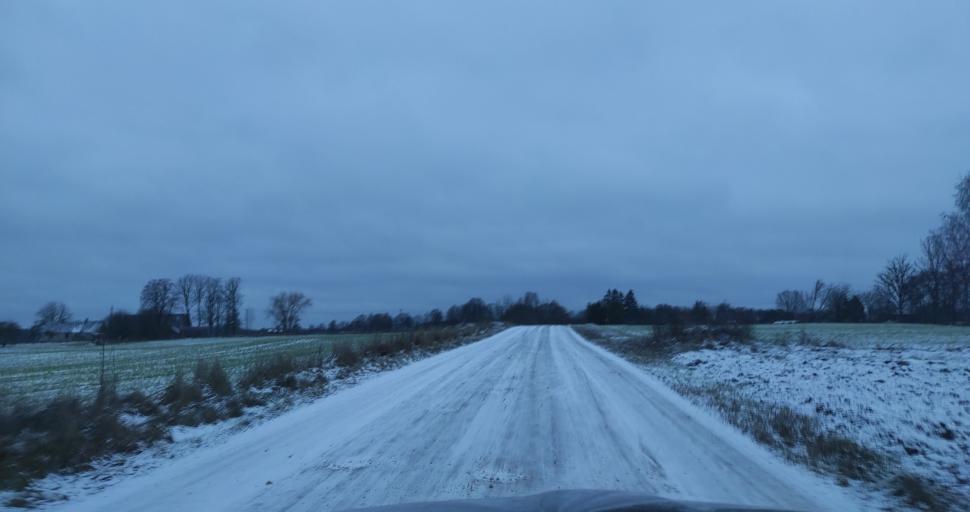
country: LV
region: Kuldigas Rajons
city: Kuldiga
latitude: 56.9666
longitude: 22.0644
